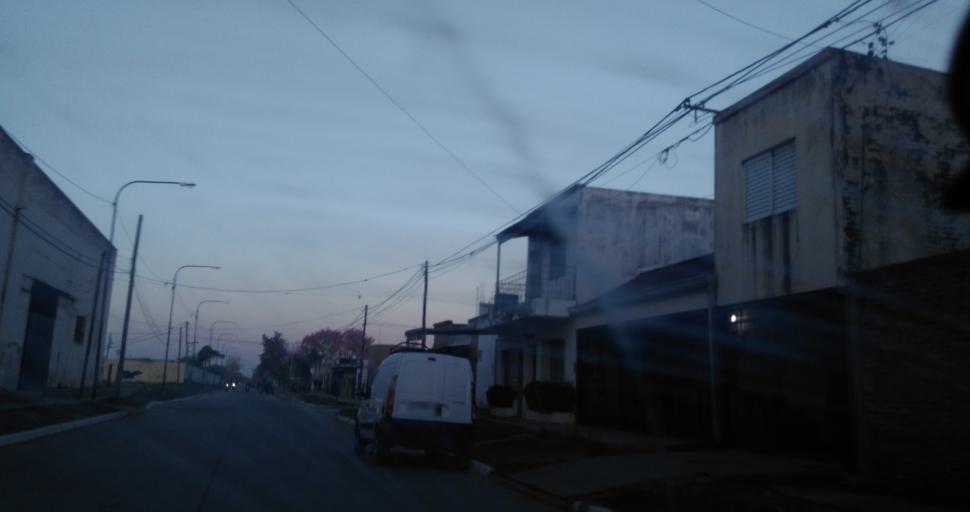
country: AR
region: Chaco
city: Resistencia
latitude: -27.4737
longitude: -58.9623
